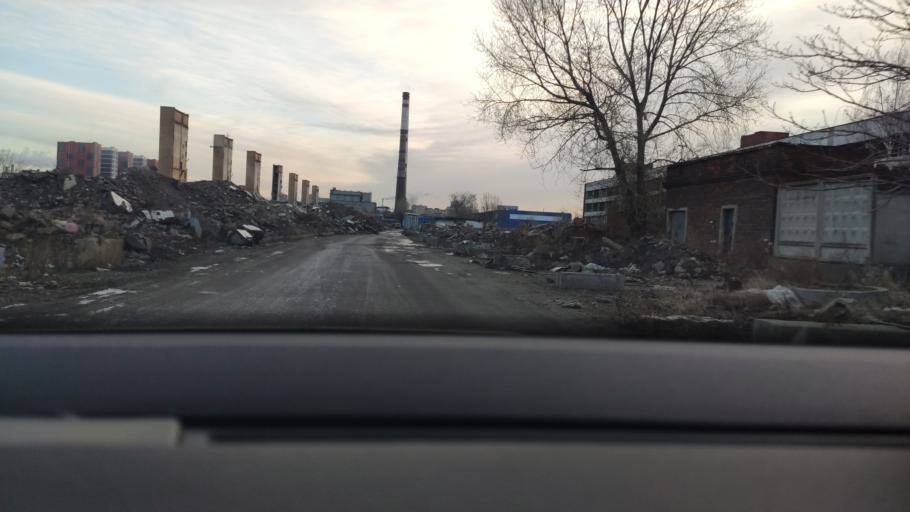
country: RU
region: Moskovskaya
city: Kozhukhovo
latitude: 55.6912
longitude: 37.6439
